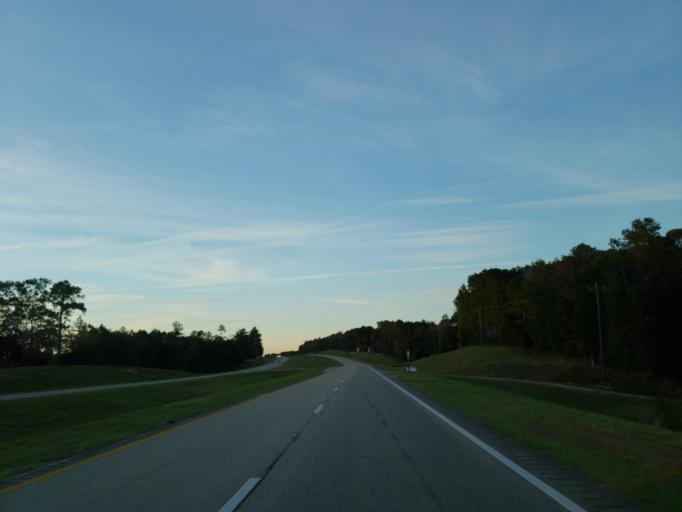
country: US
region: Mississippi
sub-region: Wayne County
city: Belmont
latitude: 31.4959
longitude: -88.4937
